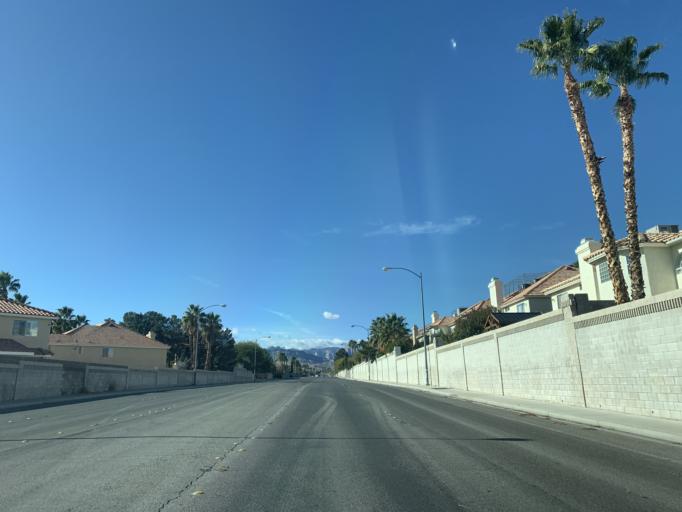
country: US
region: Nevada
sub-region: Clark County
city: Summerlin South
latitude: 36.1224
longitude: -115.2904
